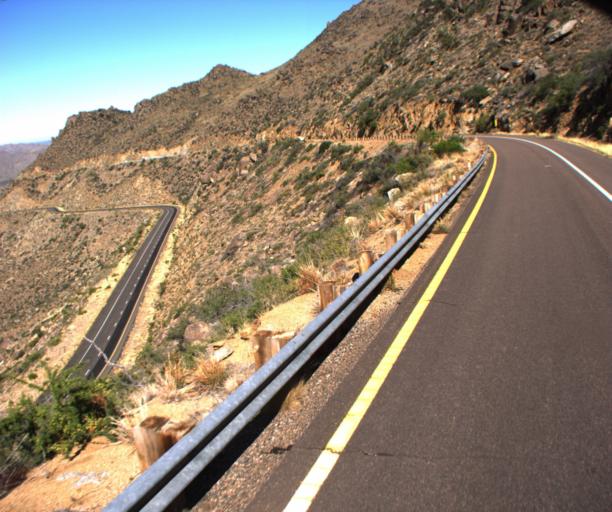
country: US
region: Arizona
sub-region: Yavapai County
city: Congress
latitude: 34.2030
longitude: -112.7670
